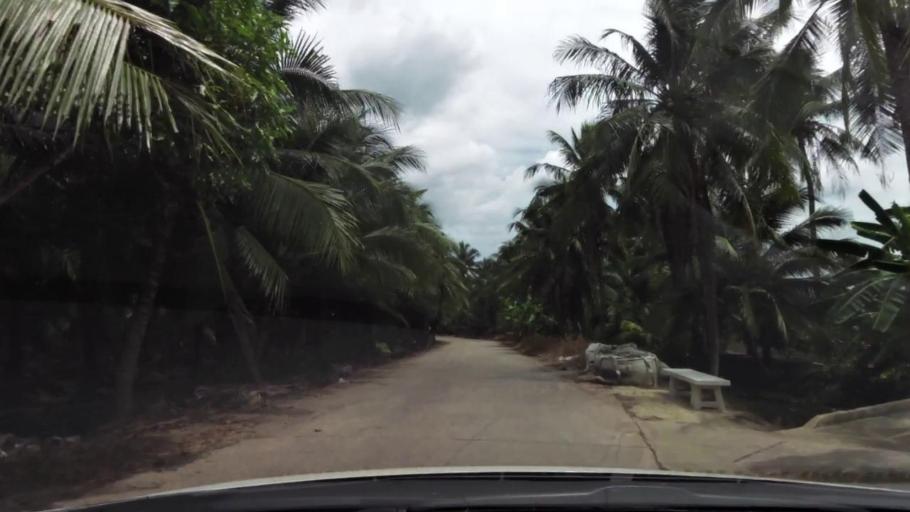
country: TH
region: Ratchaburi
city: Damnoen Saduak
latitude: 13.5217
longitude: 100.0048
